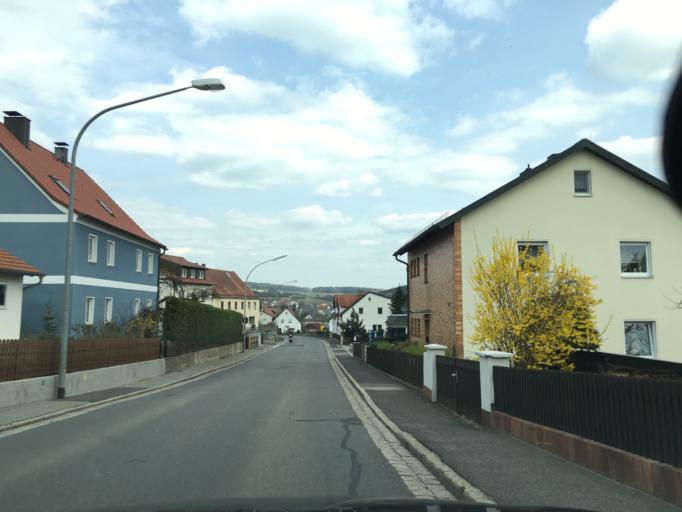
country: DE
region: Bavaria
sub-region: Upper Palatinate
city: Amberg
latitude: 49.4549
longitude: 11.8896
